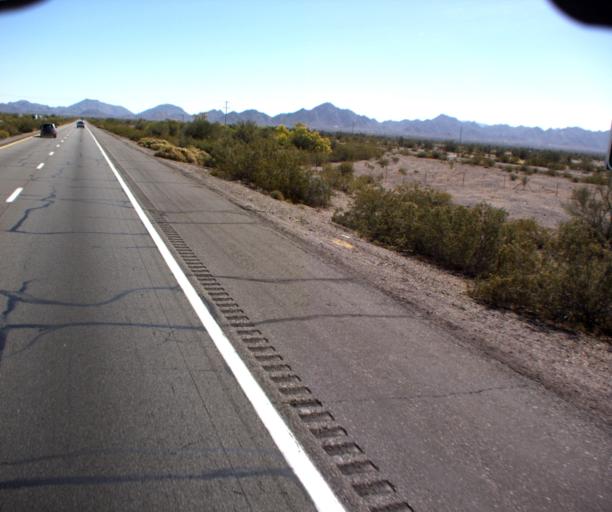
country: US
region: Arizona
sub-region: La Paz County
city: Quartzsite
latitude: 33.6672
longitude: -114.1837
